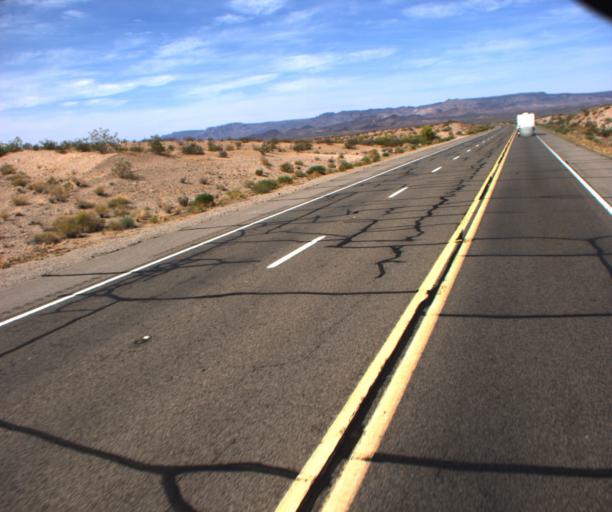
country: US
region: Arizona
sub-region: Mohave County
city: Desert Hills
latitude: 34.6826
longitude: -114.3050
